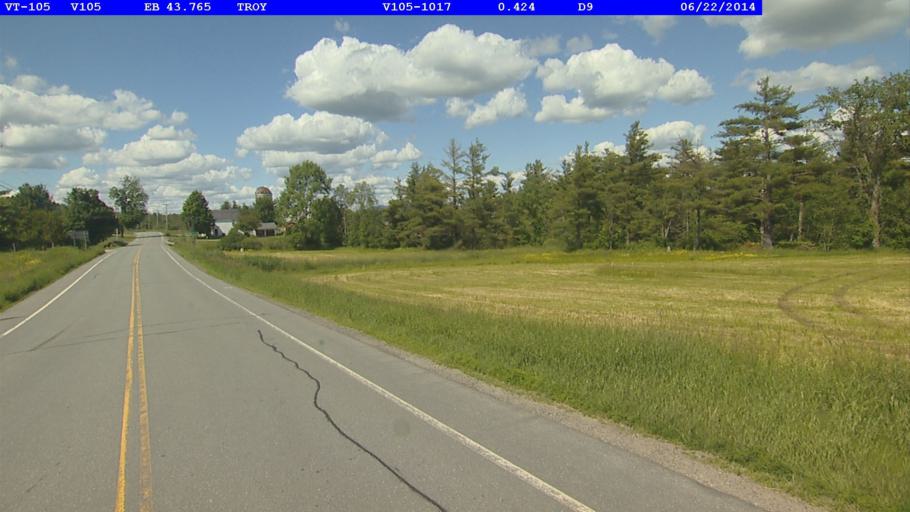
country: US
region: Vermont
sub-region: Orleans County
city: Newport
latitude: 44.9649
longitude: -72.4135
